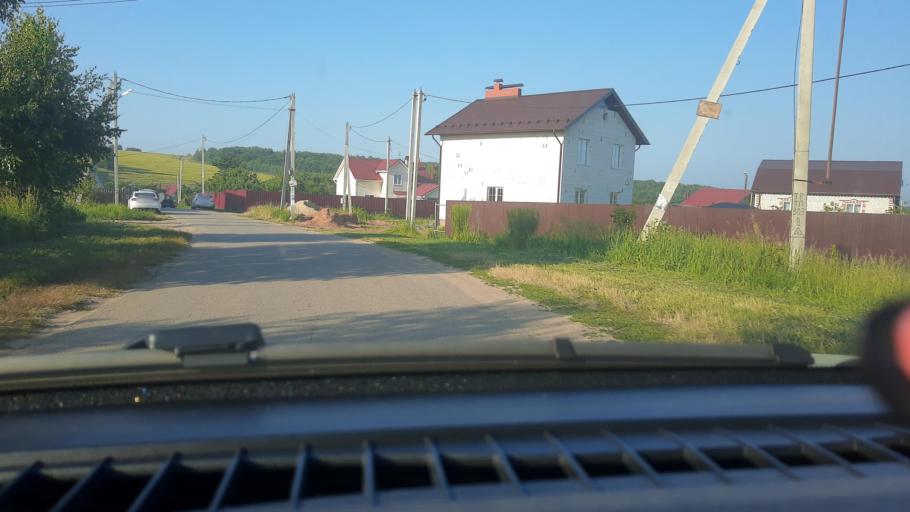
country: RU
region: Nizjnij Novgorod
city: Nizhniy Novgorod
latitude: 56.1956
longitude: 43.9574
